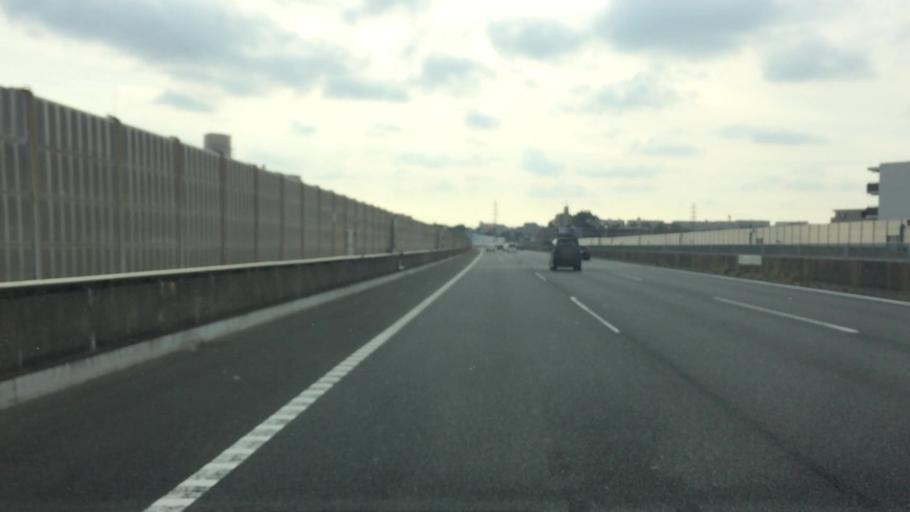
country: JP
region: Tokyo
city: Chofugaoka
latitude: 35.5924
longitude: 139.6254
